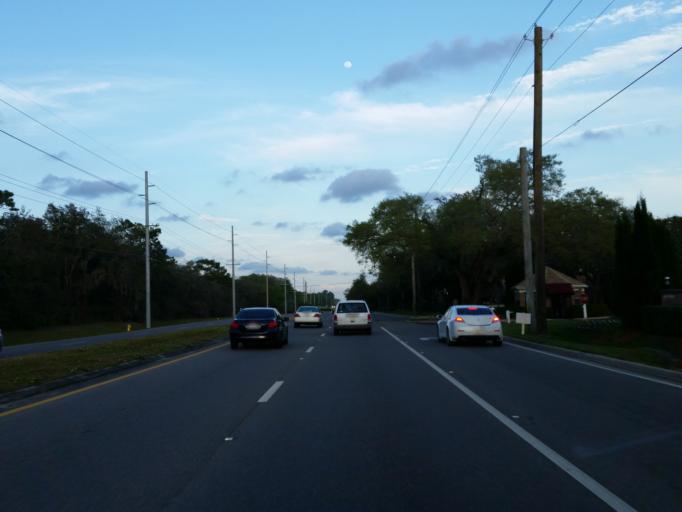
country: US
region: Florida
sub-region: Hillsborough County
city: Temple Terrace
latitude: 28.0691
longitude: -82.3841
